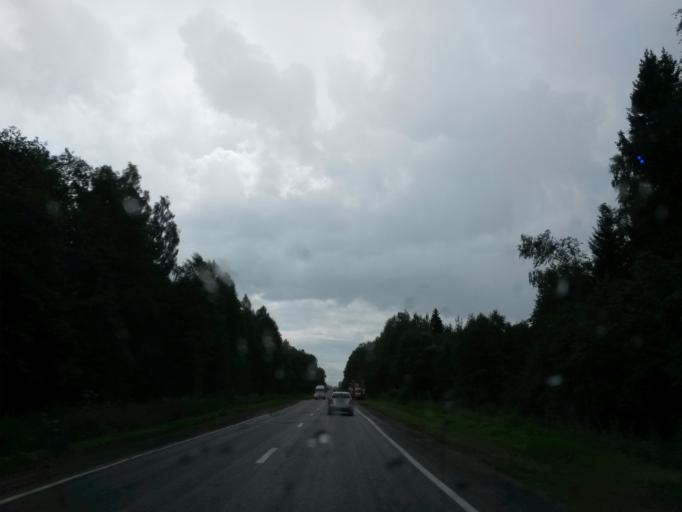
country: RU
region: Jaroslavl
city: Gavrilov-Yam
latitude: 57.4237
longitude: 39.9191
